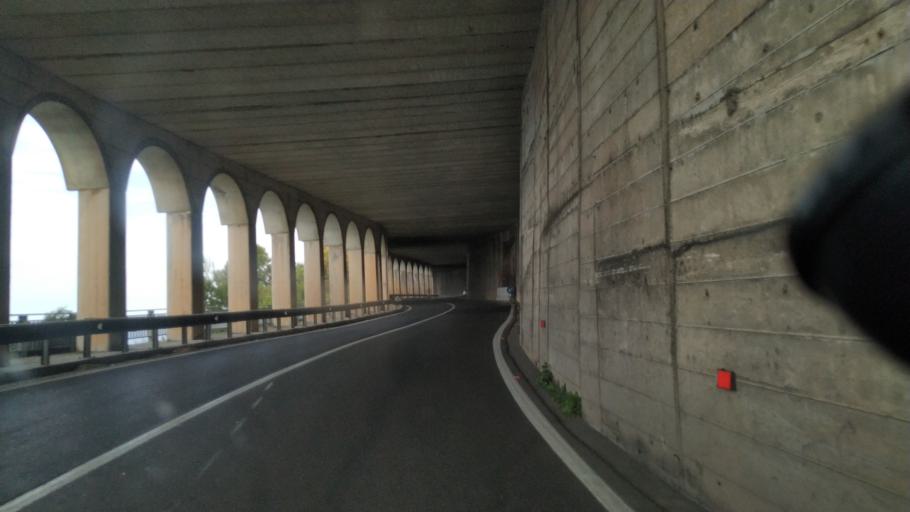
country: IT
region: Liguria
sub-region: Provincia di Savona
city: Marina di Andora
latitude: 43.9602
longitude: 8.1703
